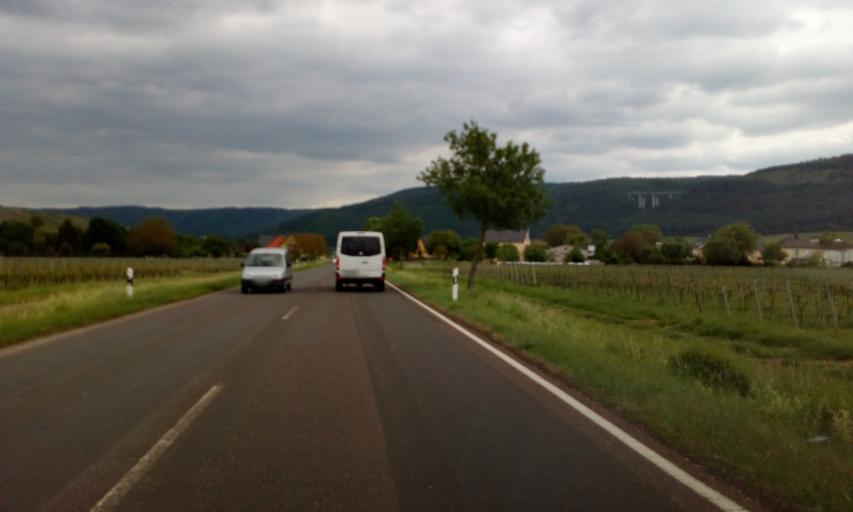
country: DE
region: Rheinland-Pfalz
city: Longuich
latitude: 49.7984
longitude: 6.7890
